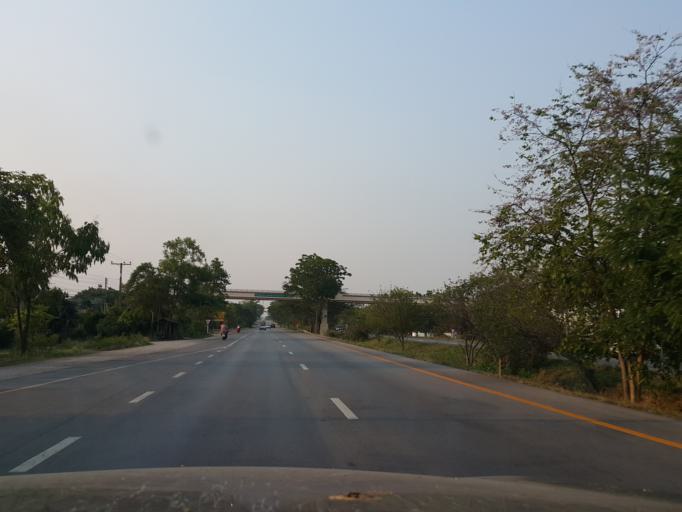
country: TH
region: Lampang
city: Sop Prap
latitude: 17.9252
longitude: 99.3458
